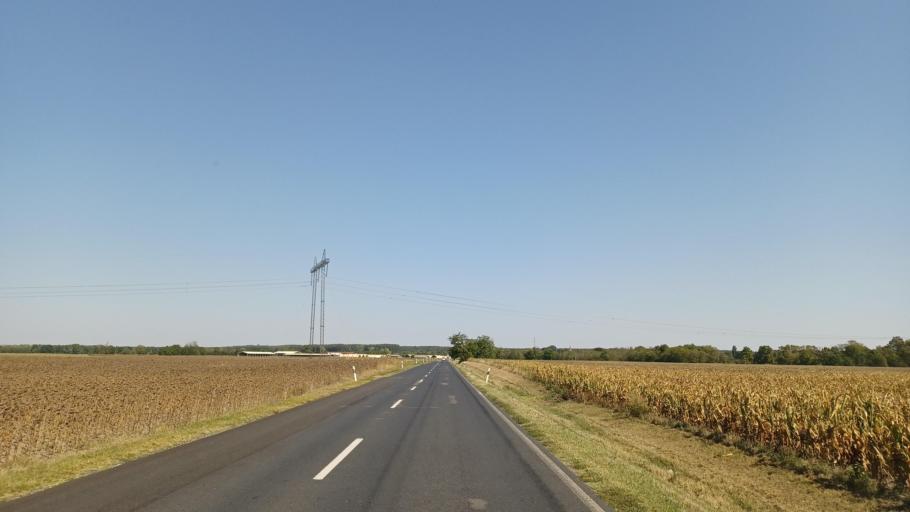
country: HU
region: Tolna
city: Nagydorog
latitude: 46.6643
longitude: 18.6559
